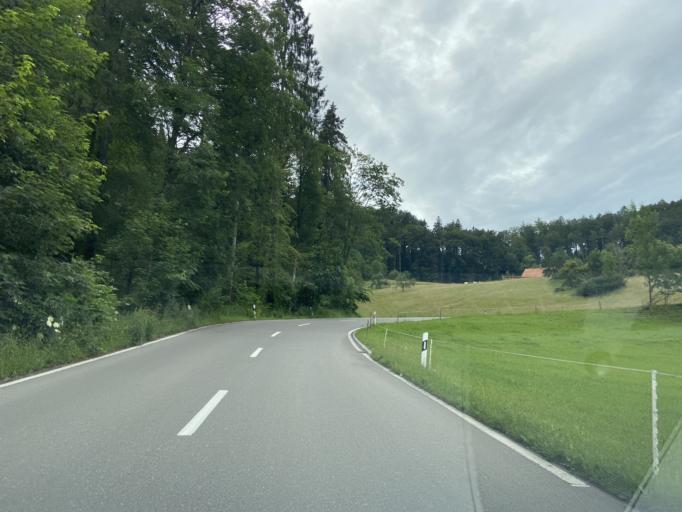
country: CH
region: Thurgau
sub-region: Muenchwilen District
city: Aadorf
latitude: 47.4595
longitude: 8.8956
